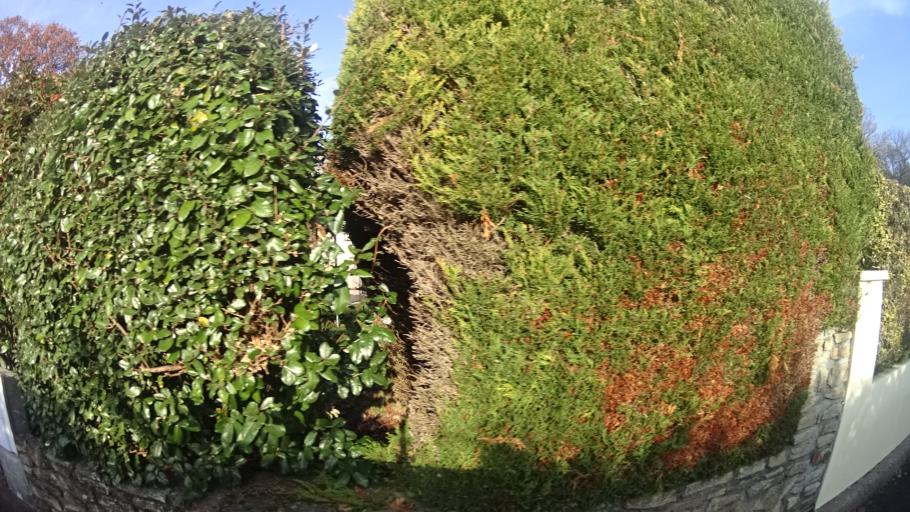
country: FR
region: Brittany
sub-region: Departement du Morbihan
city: Rieux
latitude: 47.6005
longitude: -2.1120
